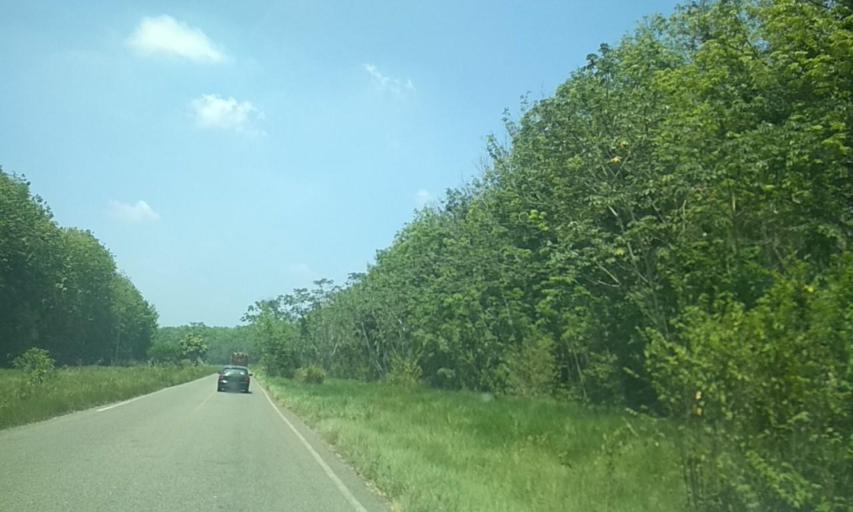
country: MX
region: Tabasco
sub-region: Huimanguillo
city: Paso de la Mina 2da. Seccion (Barrial)
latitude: 17.8120
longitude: -93.6169
